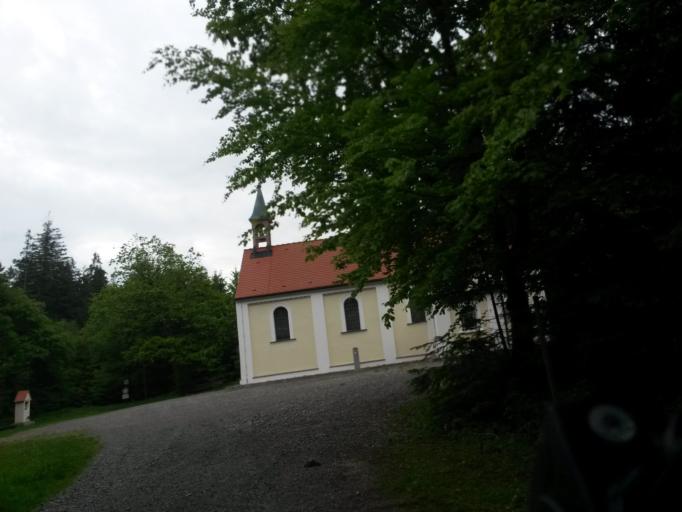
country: DE
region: Baden-Wuerttemberg
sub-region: Tuebingen Region
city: Bad Waldsee
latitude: 47.9224
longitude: 9.8219
